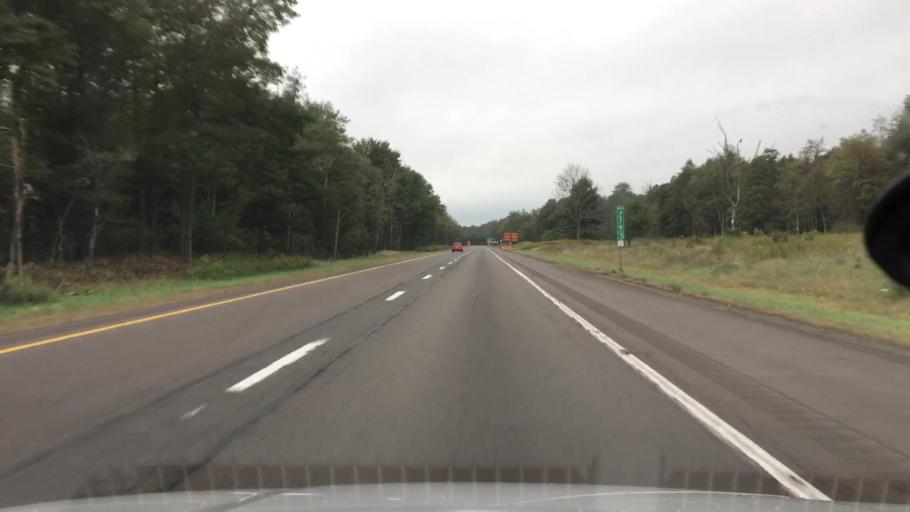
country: US
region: Pennsylvania
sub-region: Carbon County
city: Towamensing Trails
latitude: 41.0814
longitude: -75.6528
